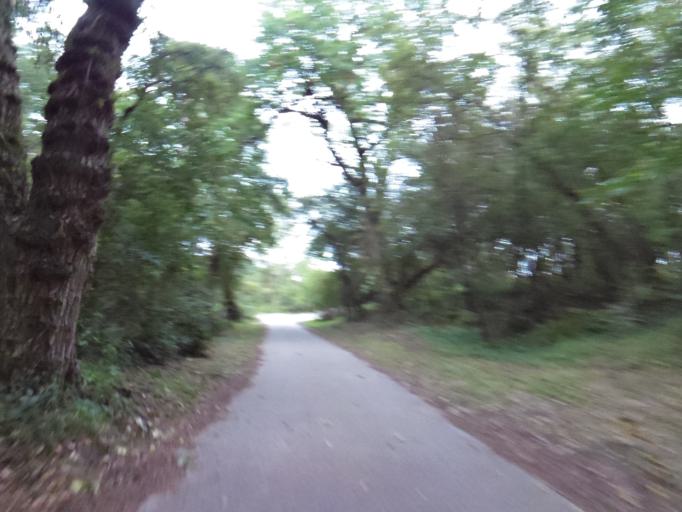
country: NL
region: South Holland
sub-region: Gemeente Leidschendam-Voorburg
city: Voorburg
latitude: 52.1230
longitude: 4.3397
